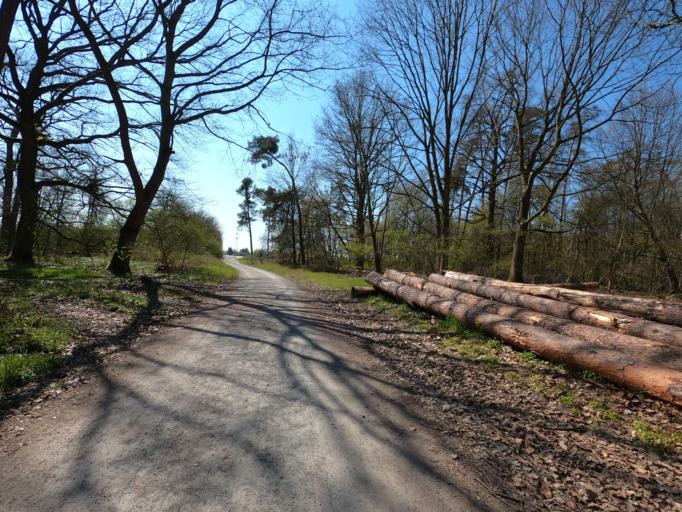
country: DE
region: Hesse
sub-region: Regierungsbezirk Darmstadt
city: Buttelborn
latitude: 49.9313
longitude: 8.5207
